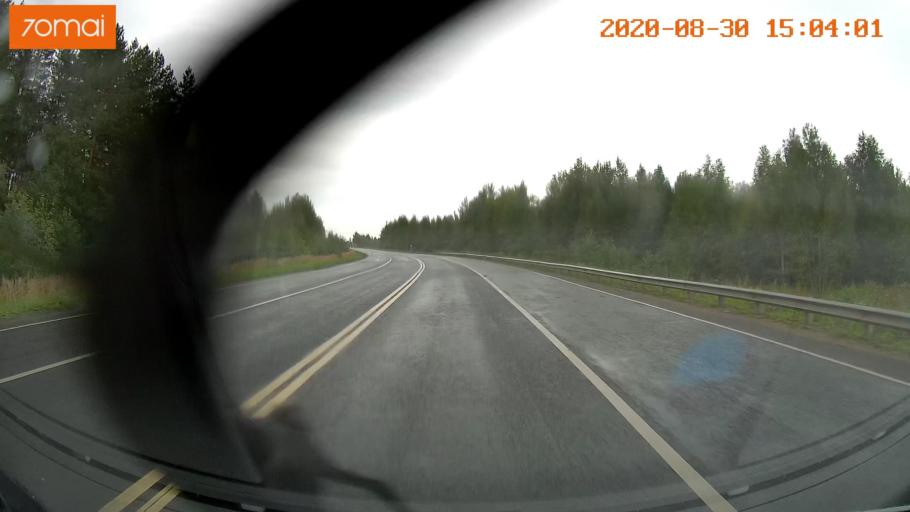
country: RU
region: Ivanovo
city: Staraya Vichuga
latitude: 57.2925
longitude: 41.9067
